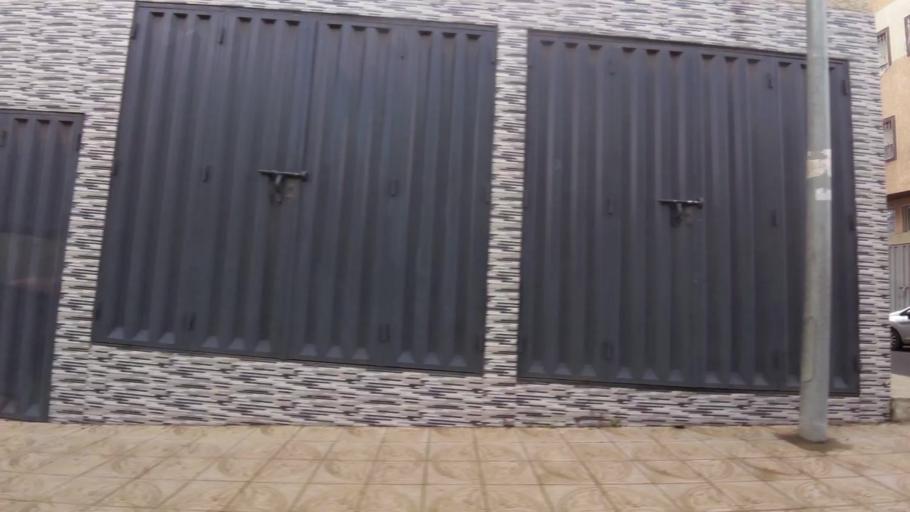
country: MA
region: Grand Casablanca
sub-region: Nouaceur
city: Bouskoura
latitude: 33.5054
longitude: -7.6508
